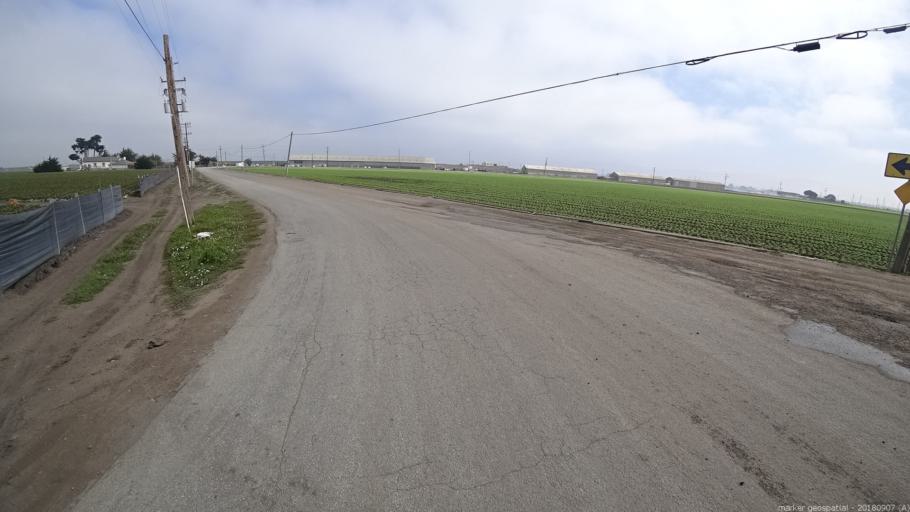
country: US
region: California
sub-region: Monterey County
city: Boronda
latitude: 36.6940
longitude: -121.7008
